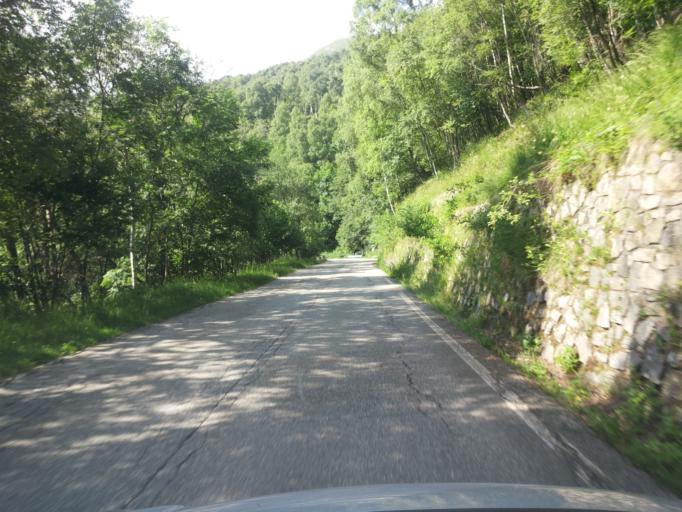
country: IT
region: Piedmont
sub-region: Provincia di Biella
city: Quittengo
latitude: 45.6555
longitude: 8.0364
